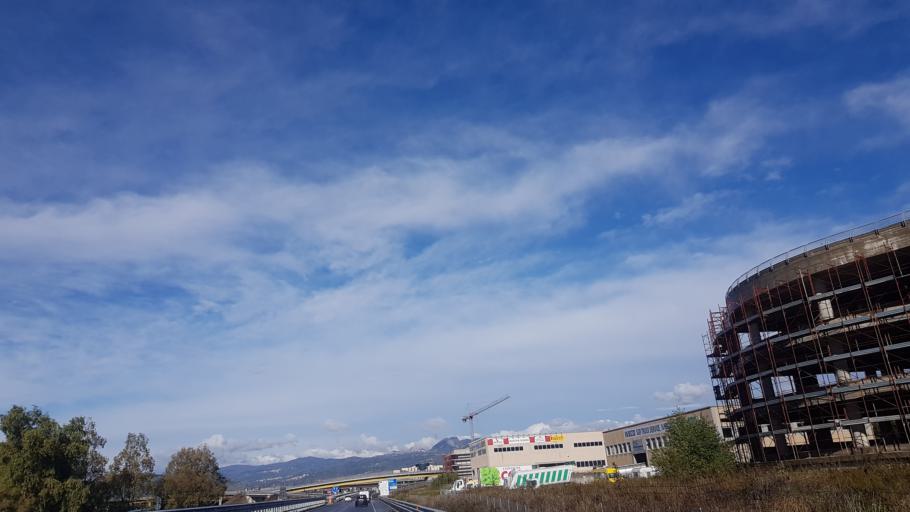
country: IT
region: Calabria
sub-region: Provincia di Catanzaro
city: Roccelletta
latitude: 38.8463
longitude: 16.5824
